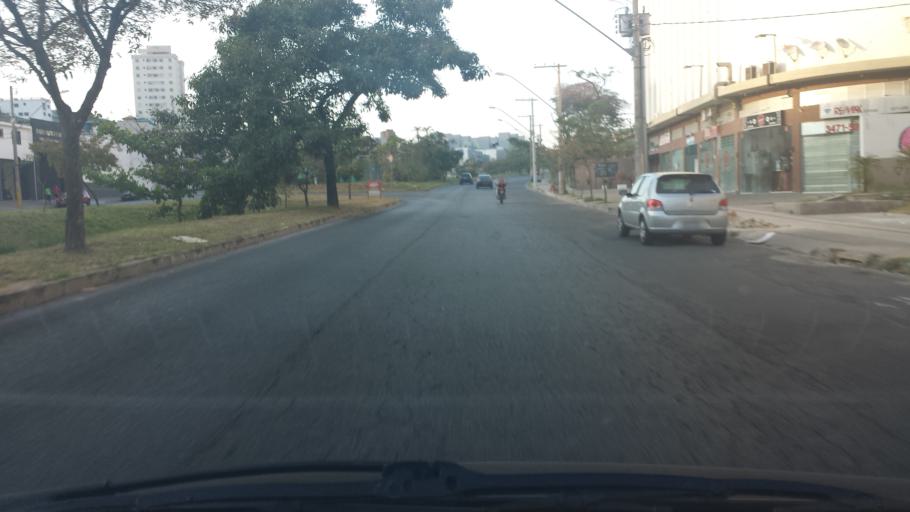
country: BR
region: Minas Gerais
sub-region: Belo Horizonte
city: Belo Horizonte
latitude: -19.8885
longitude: -43.9938
